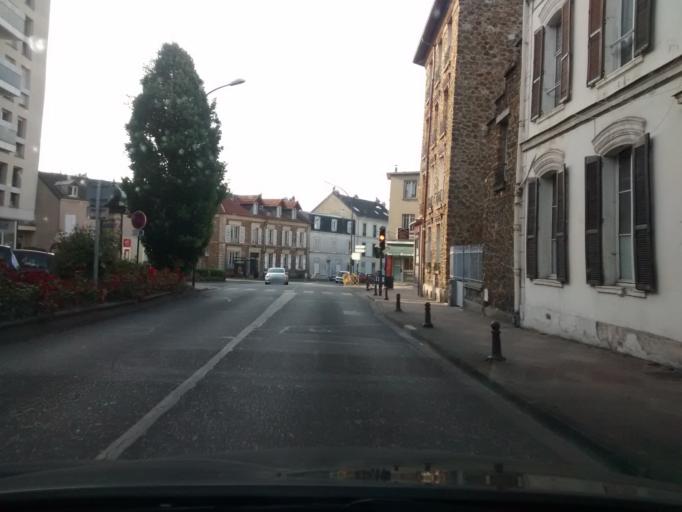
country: FR
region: Ile-de-France
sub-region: Departement des Yvelines
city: Le Chesnay
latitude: 48.8186
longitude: 2.1269
